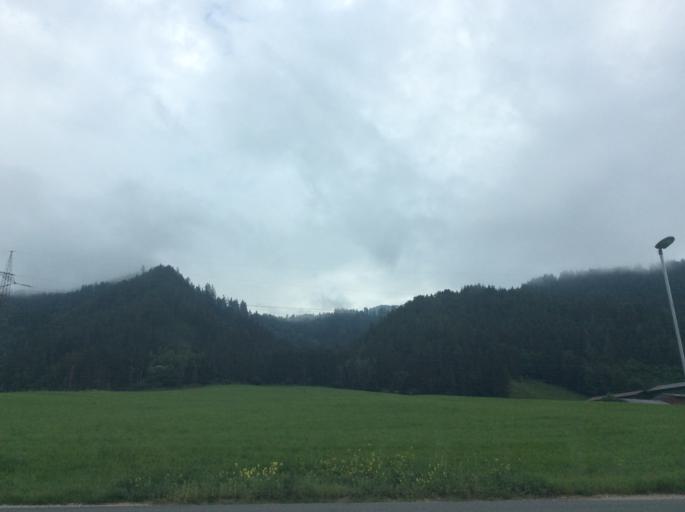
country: AT
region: Styria
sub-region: Politischer Bezirk Liezen
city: Schladming
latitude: 47.3924
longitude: 13.6671
